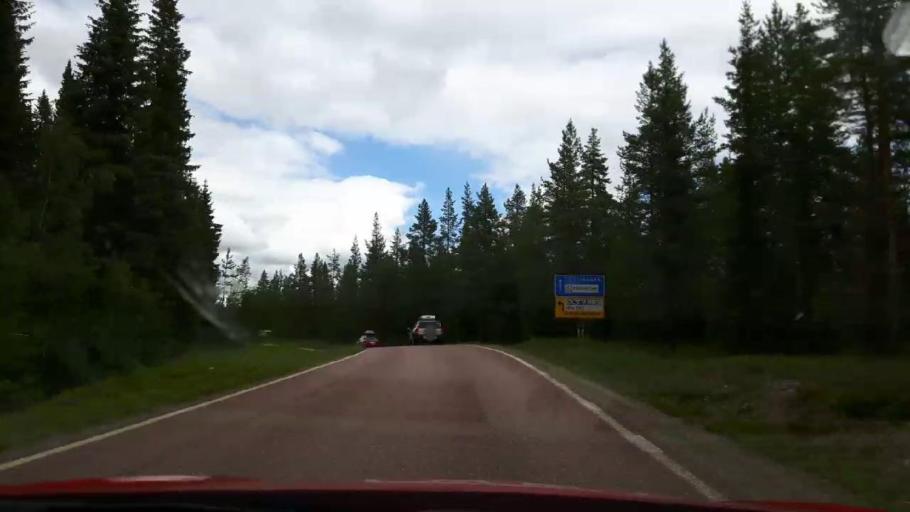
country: NO
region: Hedmark
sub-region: Trysil
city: Innbygda
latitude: 61.8627
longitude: 12.9514
